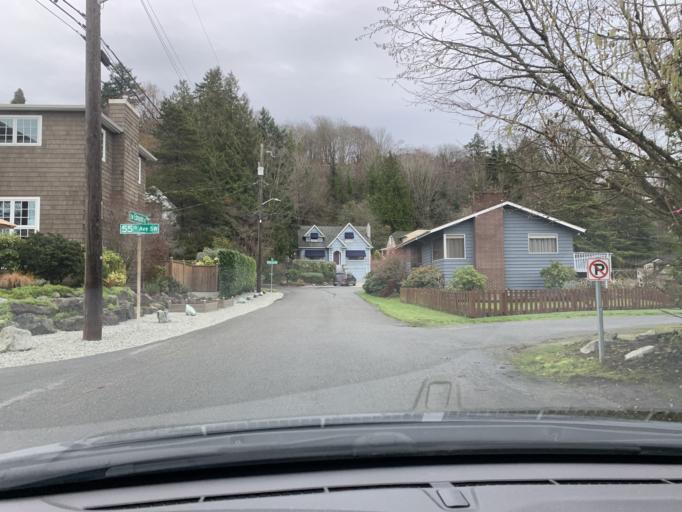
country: US
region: Washington
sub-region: King County
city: White Center
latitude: 47.5596
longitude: -122.4022
